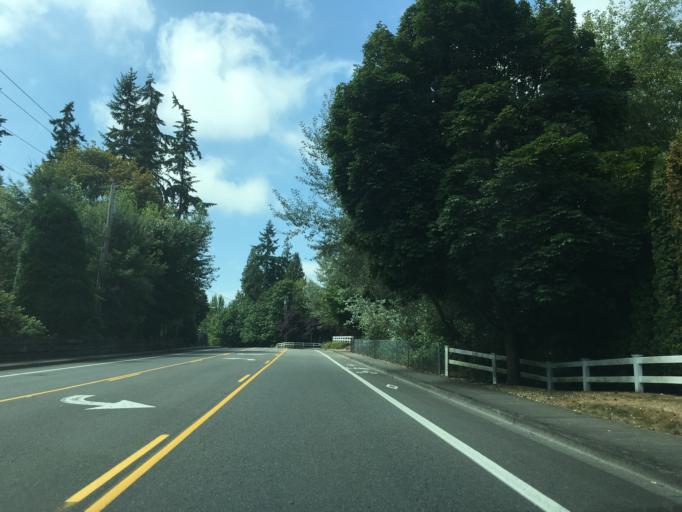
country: US
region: Washington
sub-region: King County
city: Woodinville
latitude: 47.7484
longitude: -122.1821
